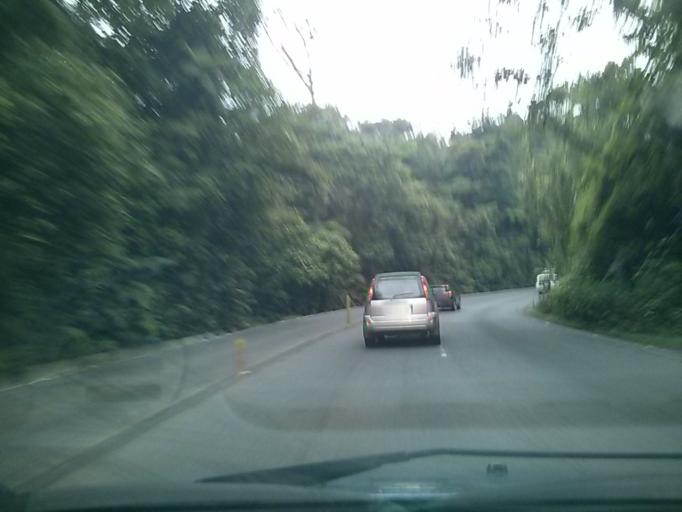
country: CR
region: San Jose
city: Dulce Nombre de Jesus
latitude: 10.1586
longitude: -83.9637
